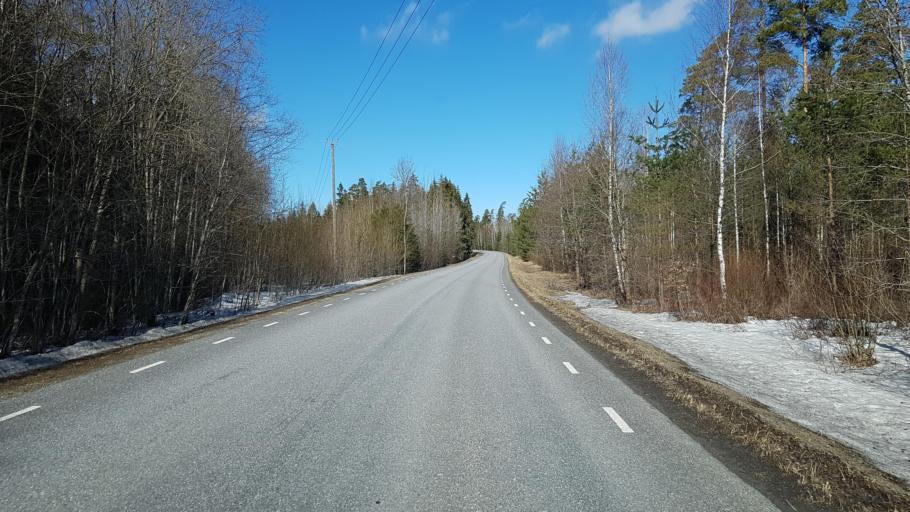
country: EE
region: Raplamaa
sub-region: Maerjamaa vald
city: Marjamaa
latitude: 58.8911
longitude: 24.4775
